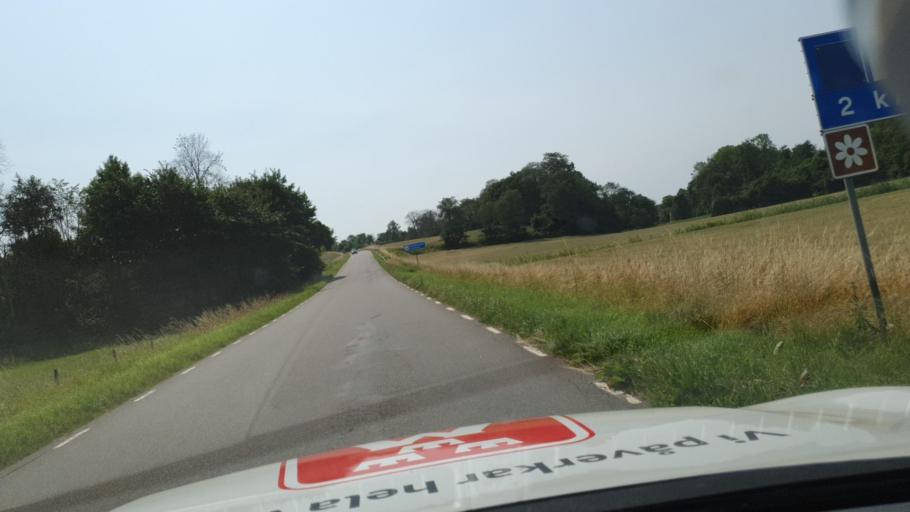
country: SE
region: Vaestra Goetaland
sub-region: Skara Kommun
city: Axvall
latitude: 58.3515
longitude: 13.6191
